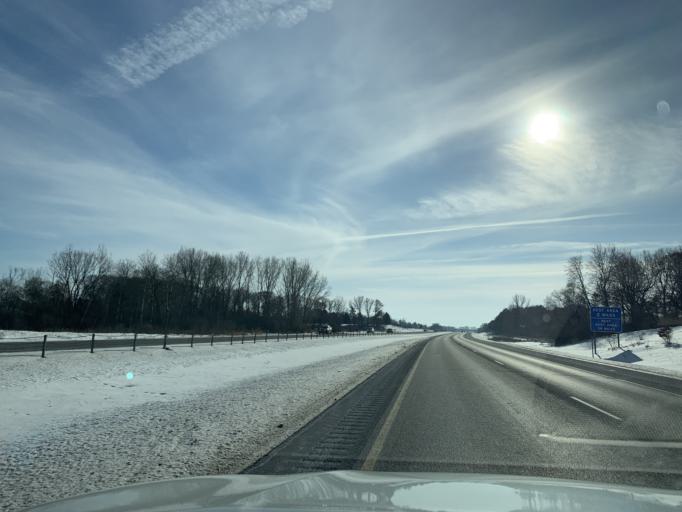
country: US
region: Minnesota
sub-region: Washington County
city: Forest Lake
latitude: 45.3025
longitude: -93.0028
